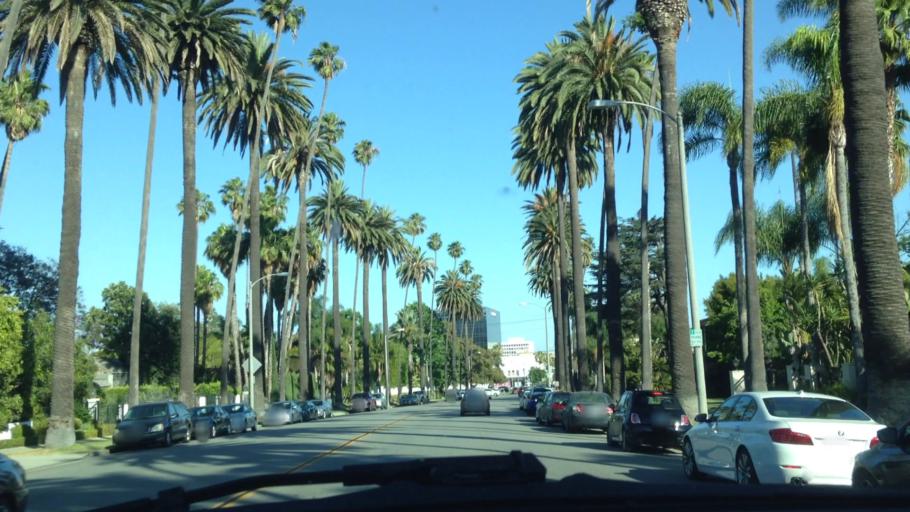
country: US
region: California
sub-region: Los Angeles County
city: Beverly Hills
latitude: 34.0737
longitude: -118.4060
